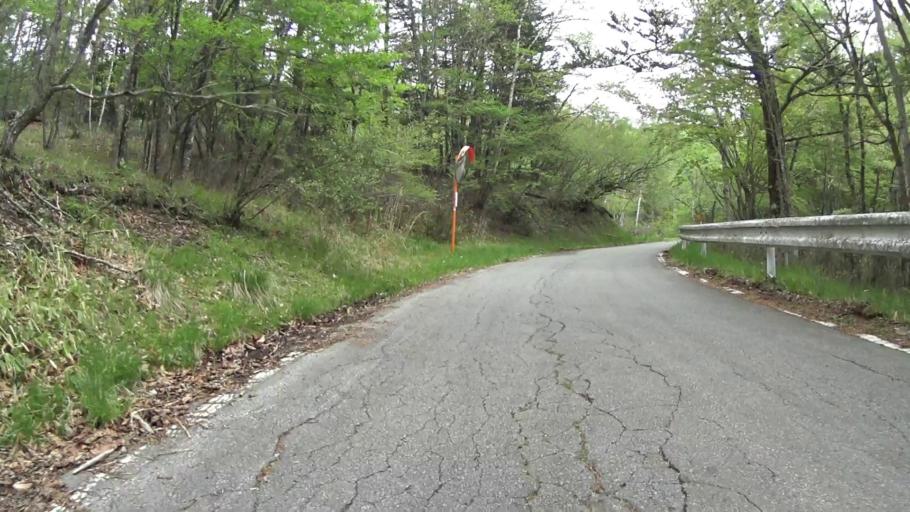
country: JP
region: Yamanashi
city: Kofu-shi
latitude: 35.8424
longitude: 138.5782
